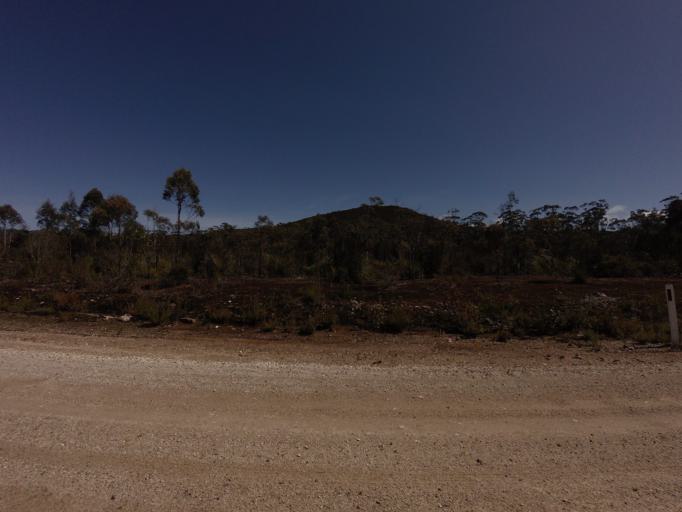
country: AU
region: Tasmania
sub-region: Huon Valley
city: Geeveston
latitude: -42.9070
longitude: 146.3675
